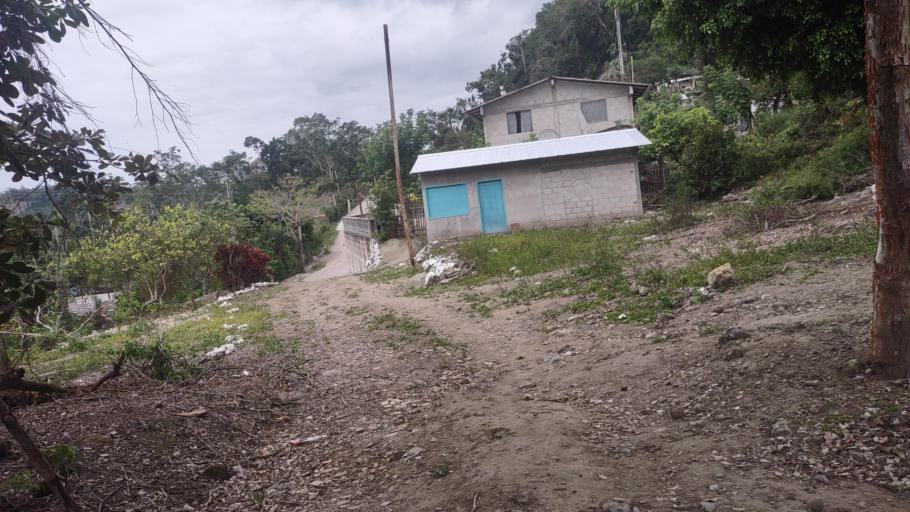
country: MX
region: Veracruz
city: Papantla de Olarte
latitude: 20.4346
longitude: -97.2640
